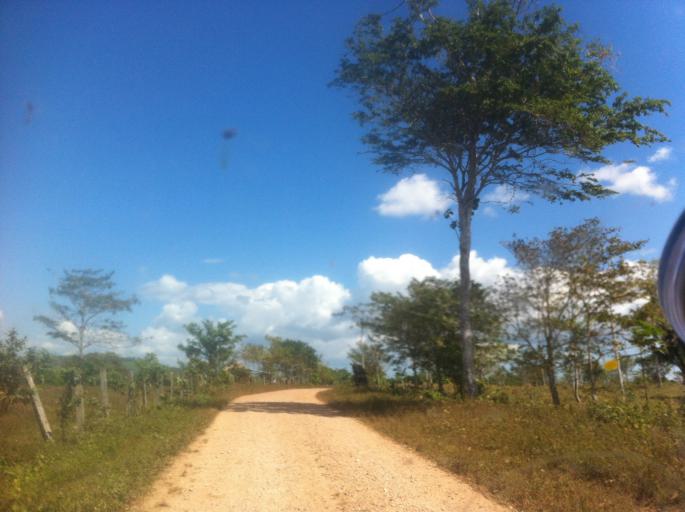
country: CR
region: Alajuela
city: Los Chiles
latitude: 11.2493
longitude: -84.4547
